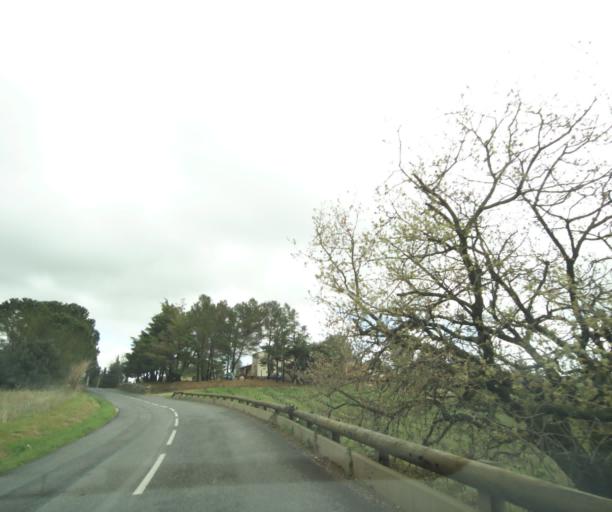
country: FR
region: Languedoc-Roussillon
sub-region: Departement de l'Herault
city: Murviel-les-Montpellier
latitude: 43.5966
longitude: 3.7456
